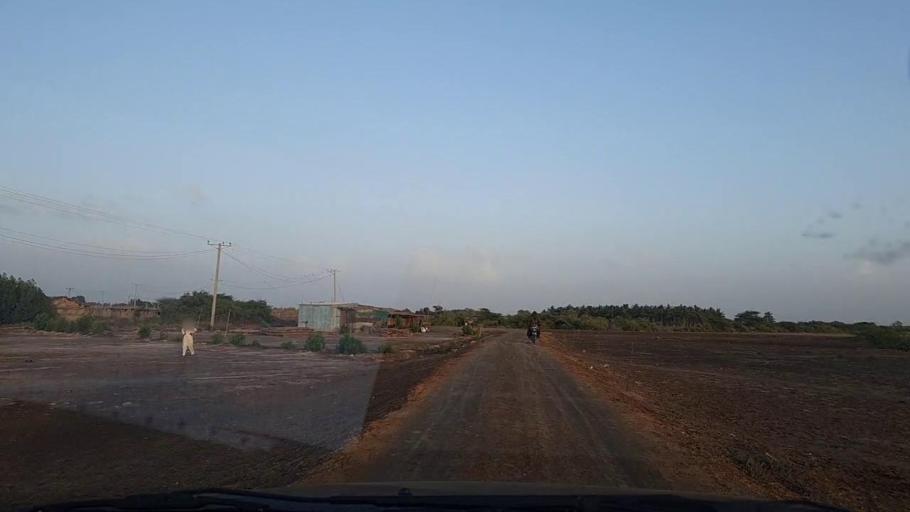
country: PK
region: Sindh
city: Keti Bandar
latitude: 24.1623
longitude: 67.6049
